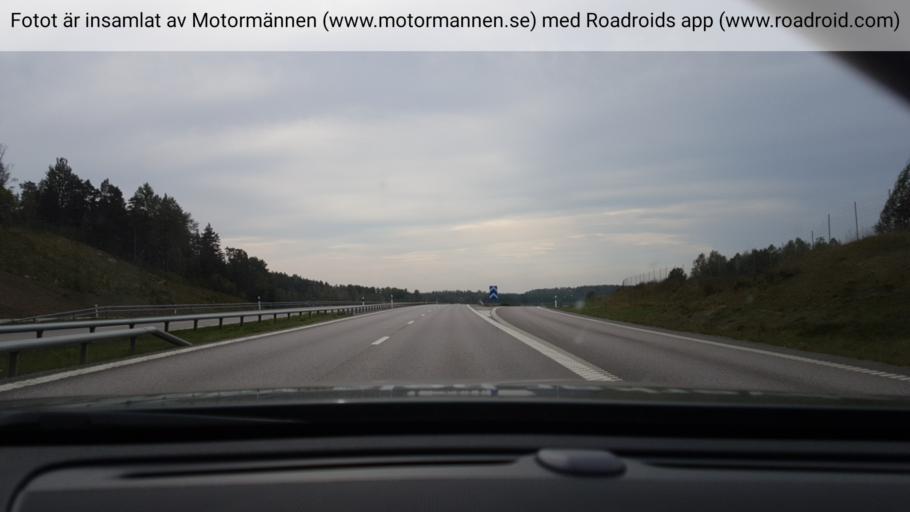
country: SE
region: Stockholm
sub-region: Nynashamns Kommun
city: Osmo
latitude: 58.9625
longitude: 17.9057
